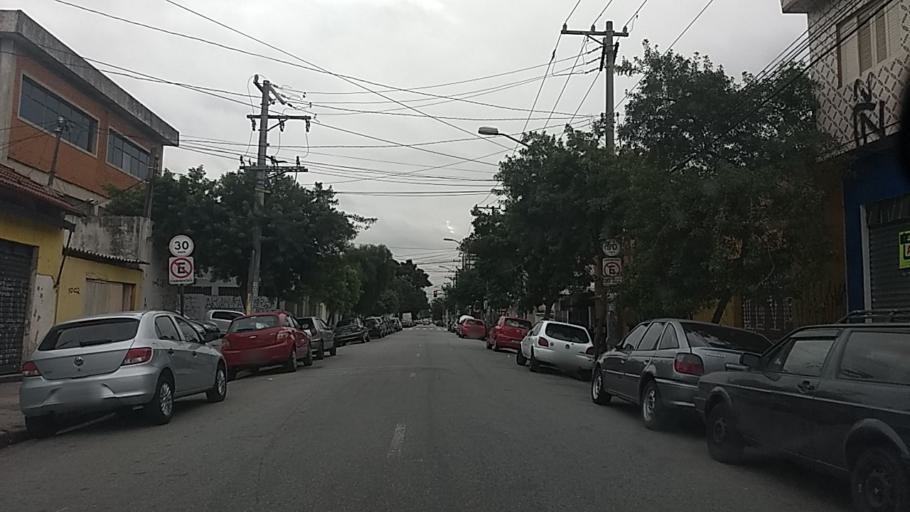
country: BR
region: Sao Paulo
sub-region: Sao Paulo
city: Sao Paulo
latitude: -23.5249
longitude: -46.5893
